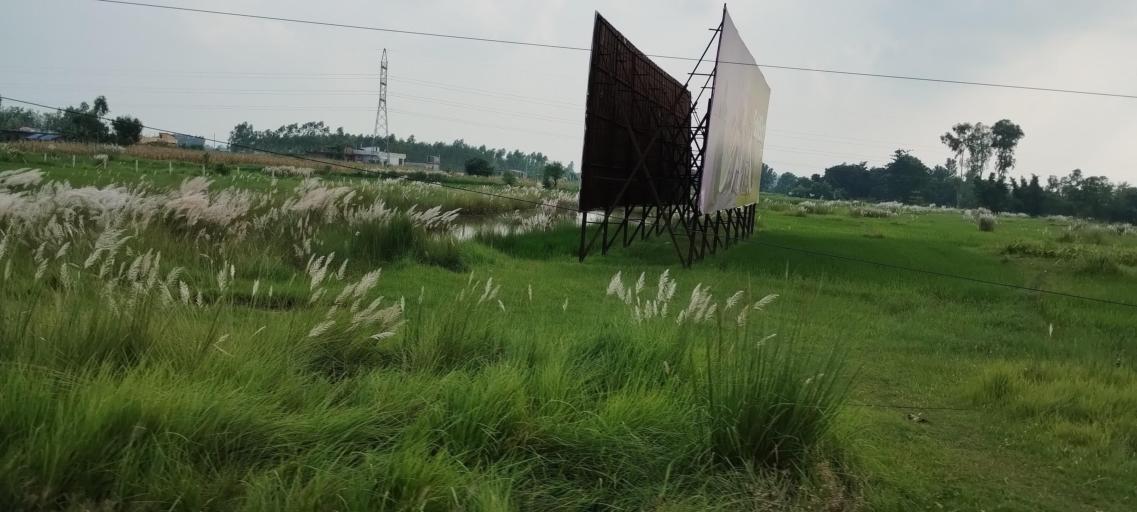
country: NP
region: Mid Western
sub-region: Bheri Zone
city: Nepalgunj
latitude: 28.1987
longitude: 81.6383
